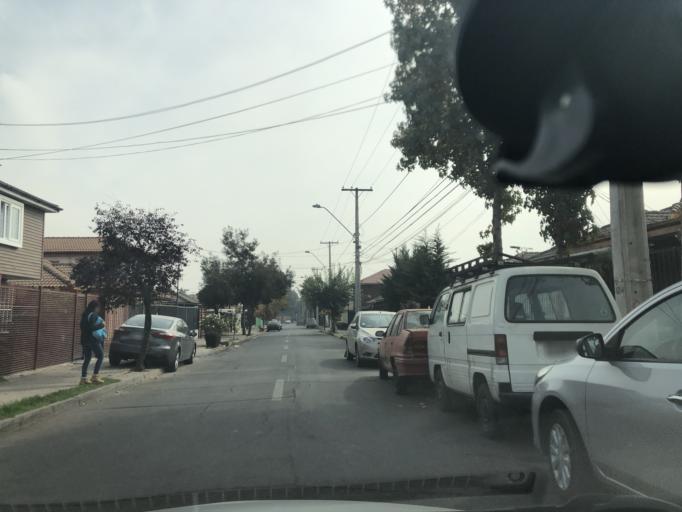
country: CL
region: Santiago Metropolitan
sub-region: Provincia de Cordillera
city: Puente Alto
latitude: -33.5640
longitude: -70.5612
